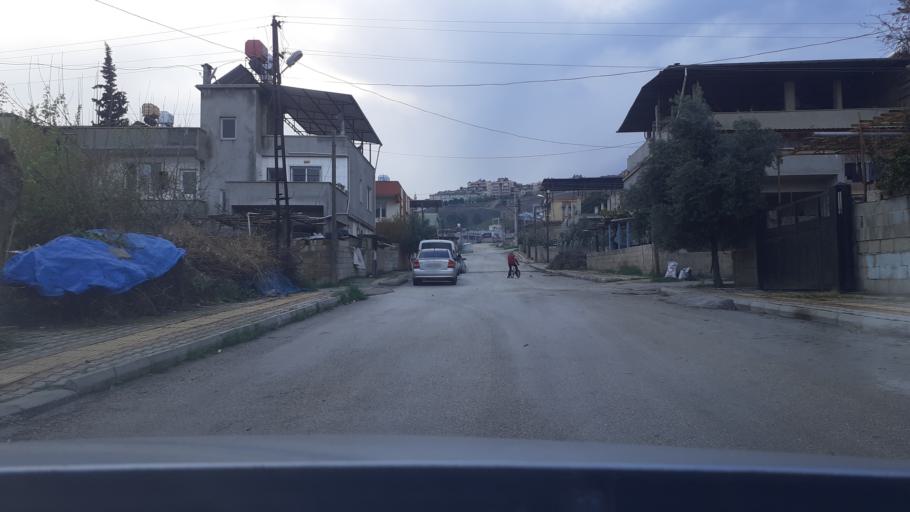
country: TR
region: Hatay
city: Kirikhan
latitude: 36.4834
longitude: 36.3481
